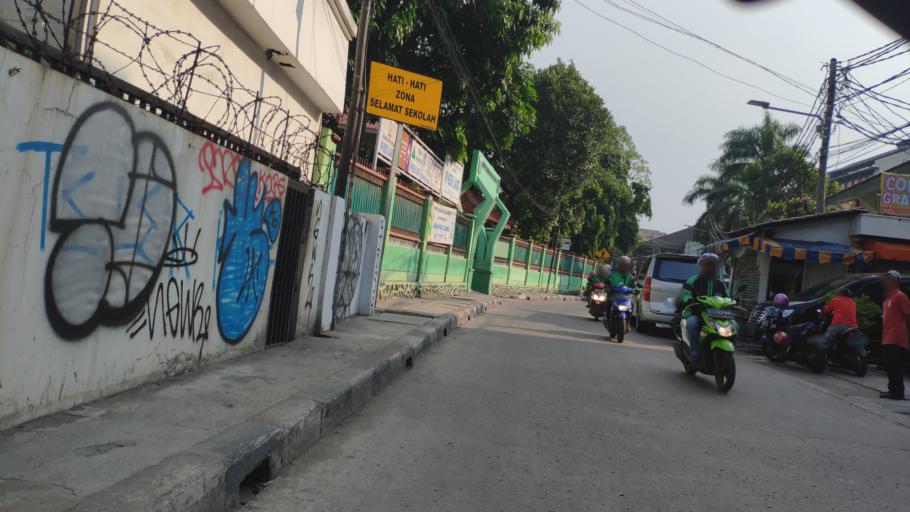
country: ID
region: Jakarta Raya
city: Jakarta
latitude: -6.2779
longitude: 106.7998
